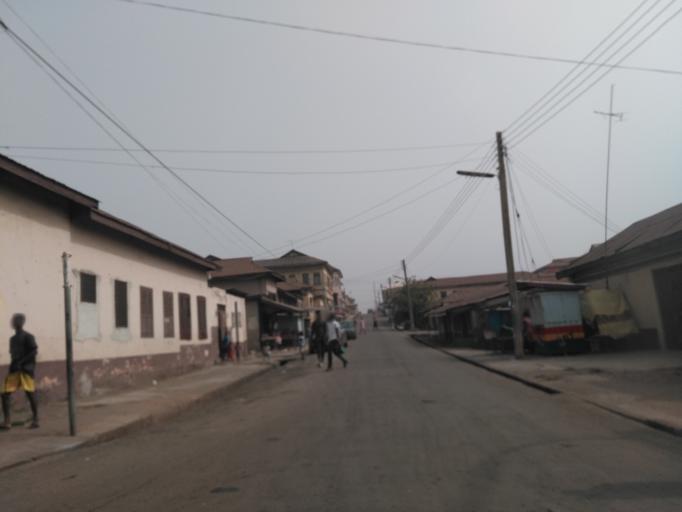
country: GH
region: Ashanti
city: Kumasi
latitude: 6.7039
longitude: -1.6222
